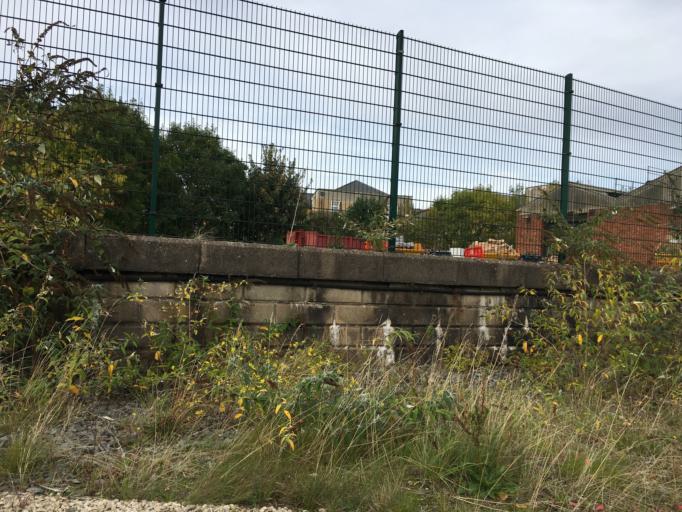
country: GB
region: England
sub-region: City of York
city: York
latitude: 53.9594
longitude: -1.0998
